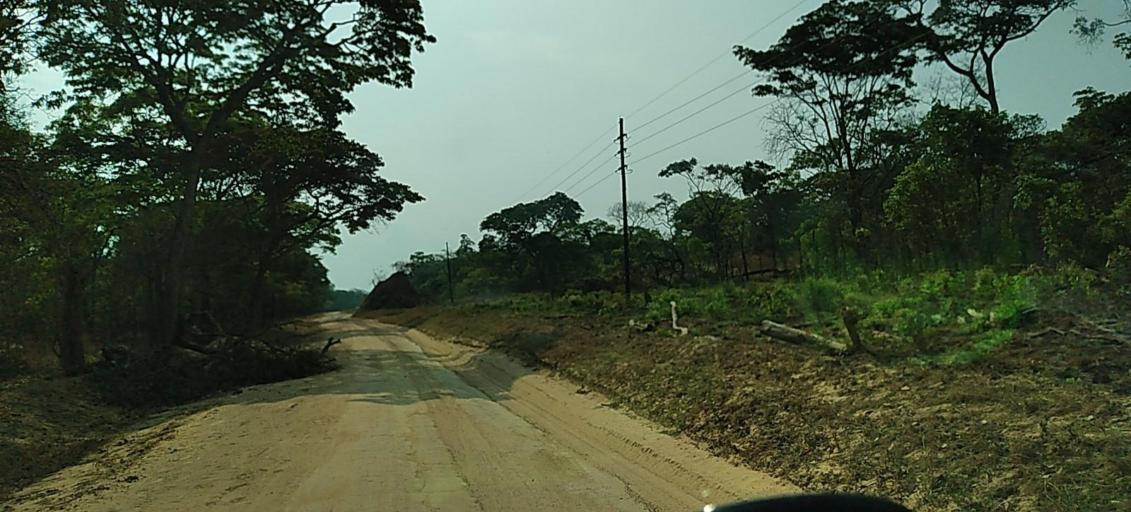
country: ZM
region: North-Western
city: Solwezi
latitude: -12.6819
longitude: 26.3852
